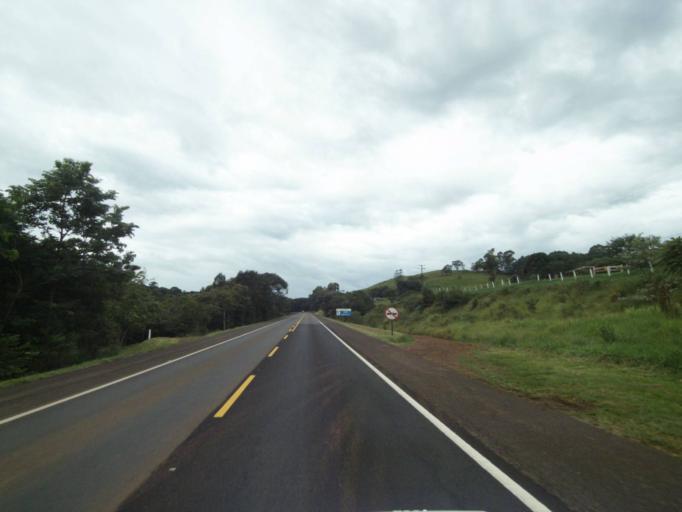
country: BR
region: Parana
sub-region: Guaraniacu
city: Guaraniacu
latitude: -25.1109
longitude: -52.8483
